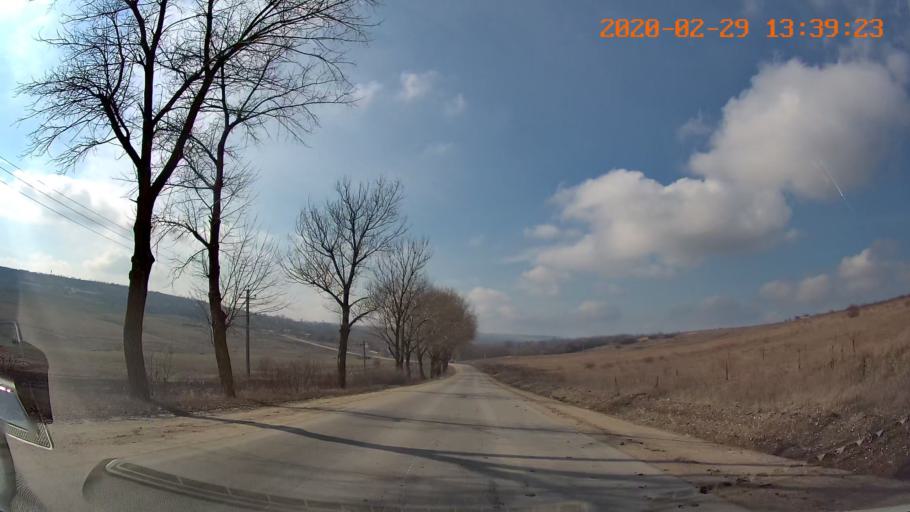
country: MD
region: Floresti
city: Leninskiy
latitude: 47.8515
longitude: 28.5823
